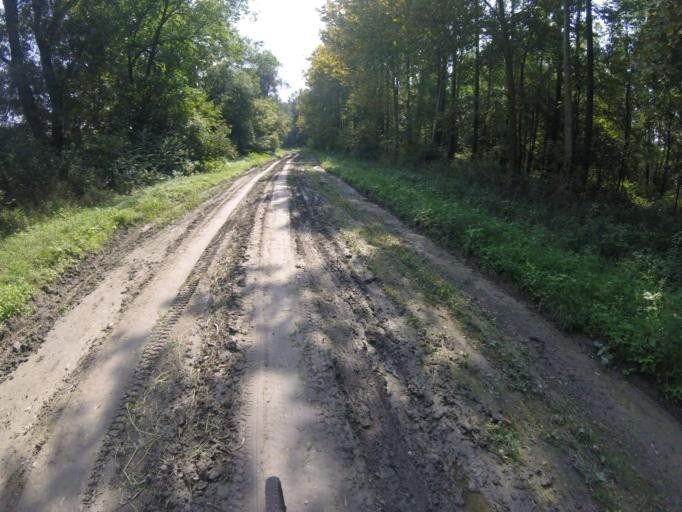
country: HU
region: Bacs-Kiskun
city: Baja
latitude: 46.1978
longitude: 18.9022
